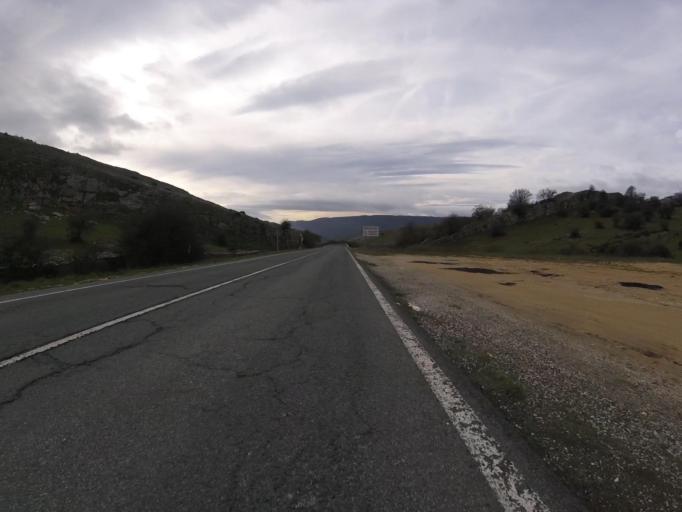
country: ES
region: Navarre
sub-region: Provincia de Navarra
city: Arbizu
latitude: 42.8586
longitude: -2.0121
